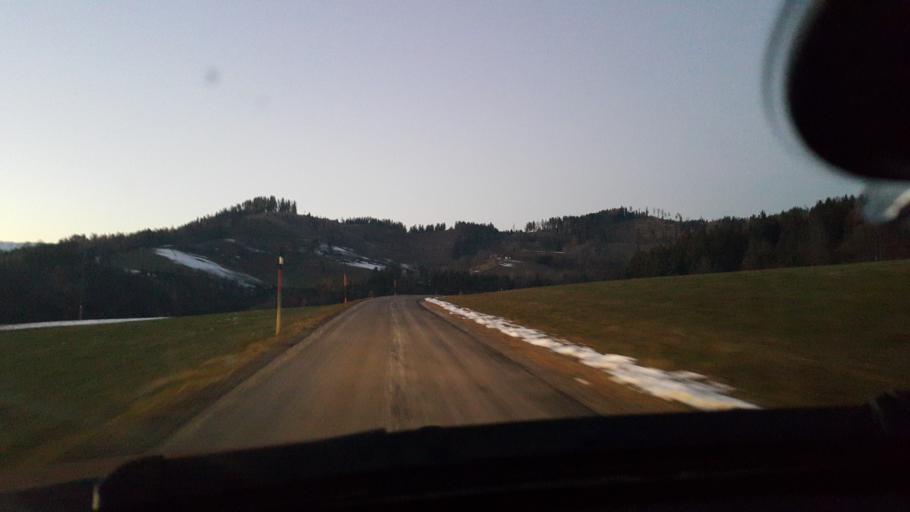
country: AT
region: Styria
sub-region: Politischer Bezirk Graz-Umgebung
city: Stiwoll
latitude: 47.1203
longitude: 15.2203
